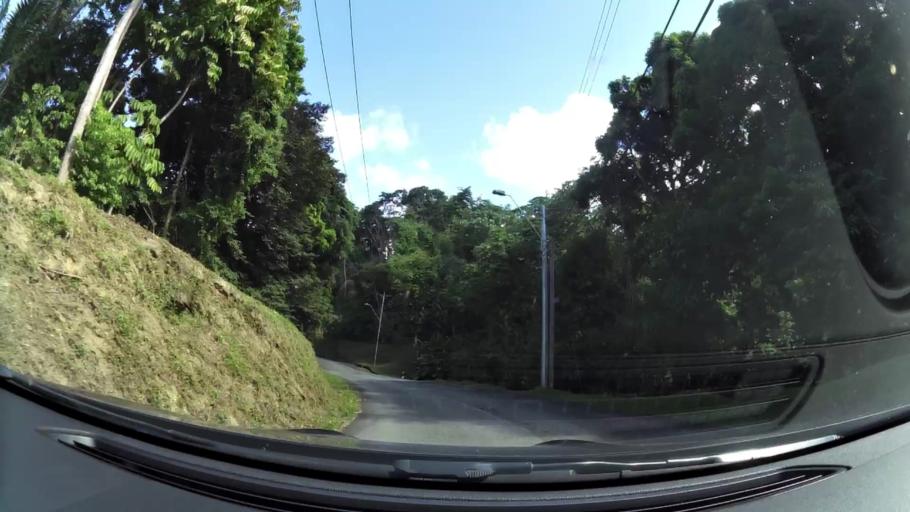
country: TT
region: Eastern Tobago
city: Roxborough
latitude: 11.3117
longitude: -60.6237
